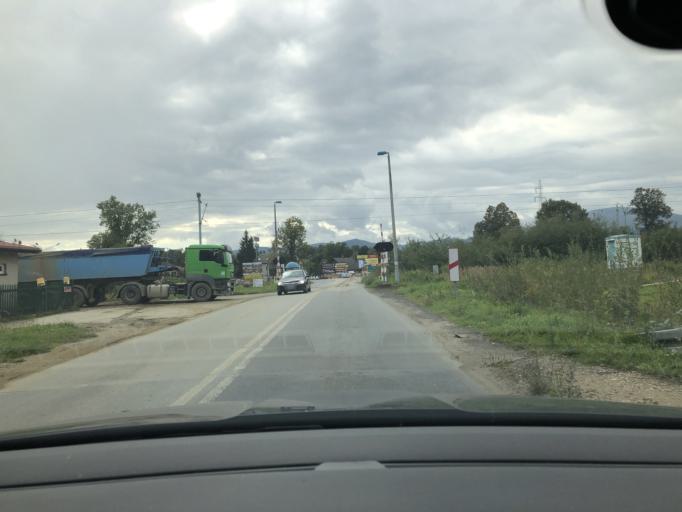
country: PL
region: Silesian Voivodeship
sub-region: Powiat zywiecki
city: Zarzecze
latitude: 49.7135
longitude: 19.1647
